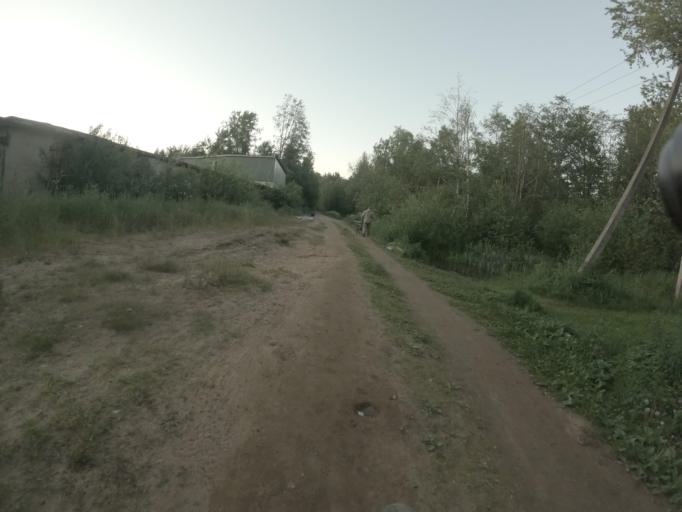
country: RU
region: St.-Petersburg
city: Krasnogvargeisky
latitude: 59.9863
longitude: 30.5297
